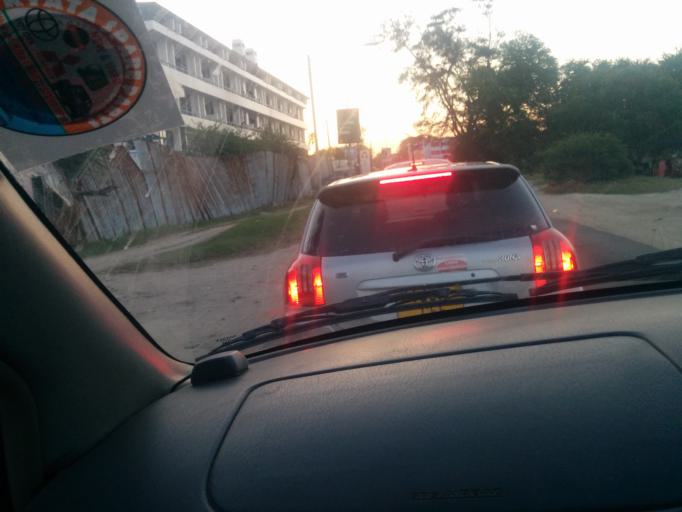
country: TZ
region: Dar es Salaam
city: Dar es Salaam
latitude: -6.8040
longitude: 39.2892
